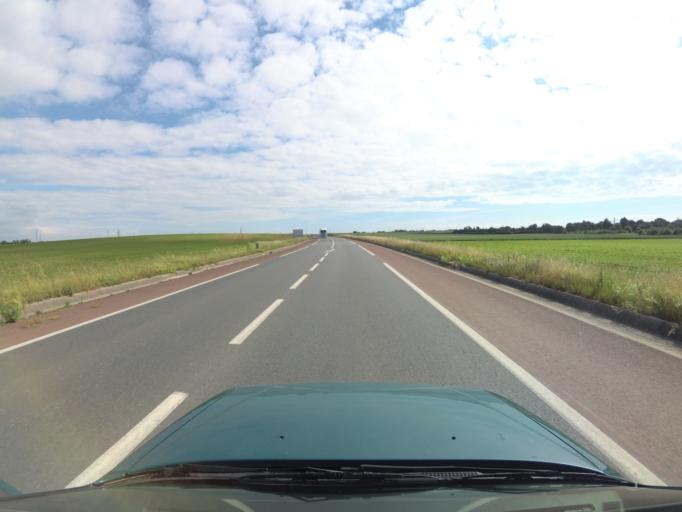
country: FR
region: Poitou-Charentes
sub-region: Departement de la Charente-Maritime
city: Saint-Xandre
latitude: 46.2153
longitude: -1.0905
